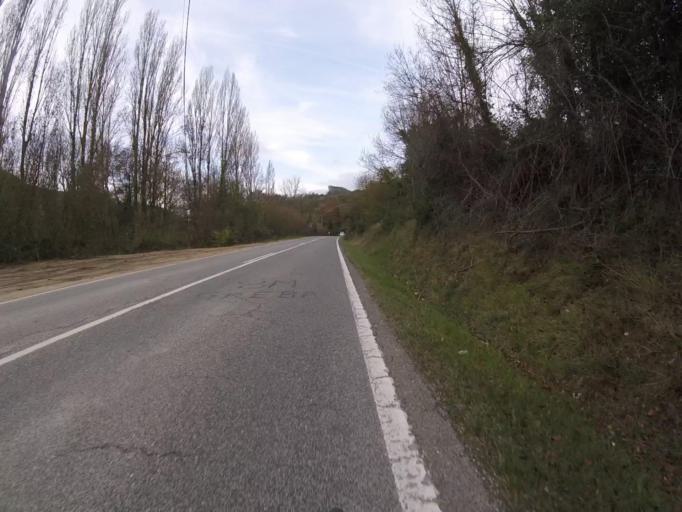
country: ES
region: Navarre
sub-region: Provincia de Navarra
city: Estella
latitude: 42.6963
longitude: -2.0502
